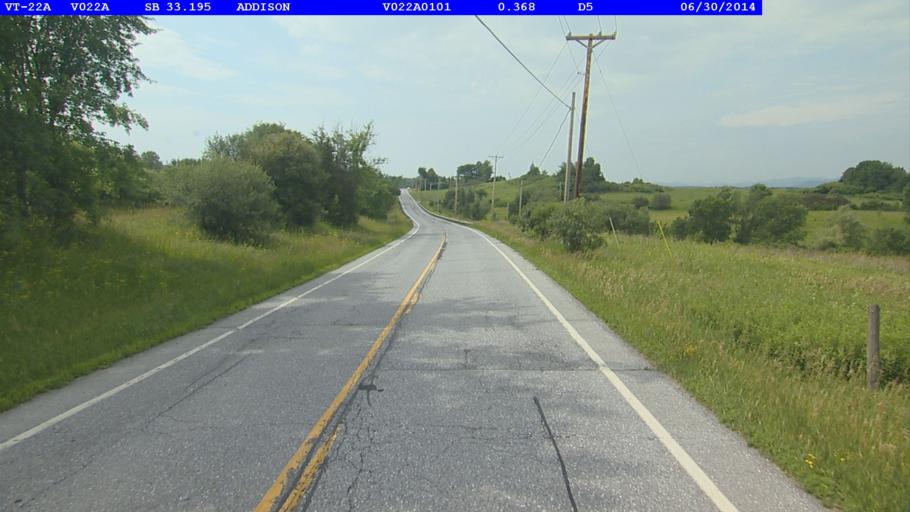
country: US
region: Vermont
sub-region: Addison County
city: Middlebury (village)
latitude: 44.0352
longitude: -73.3074
